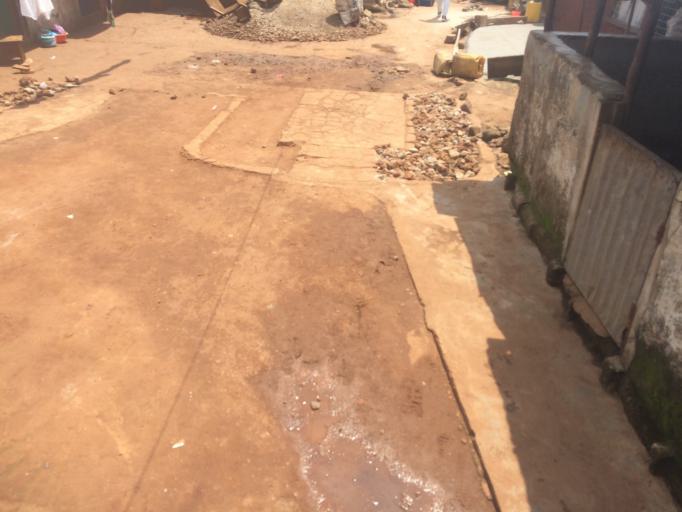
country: SL
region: Western Area
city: Freetown
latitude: 8.4789
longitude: -13.2002
